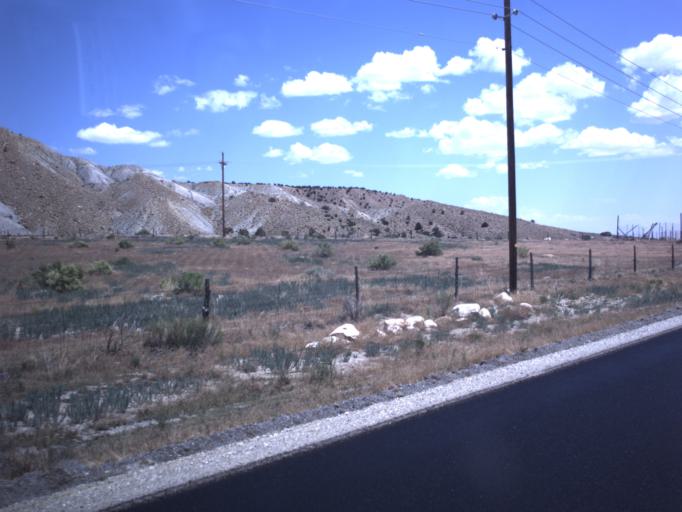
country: US
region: Utah
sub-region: Emery County
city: Orangeville
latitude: 39.2560
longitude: -111.1000
